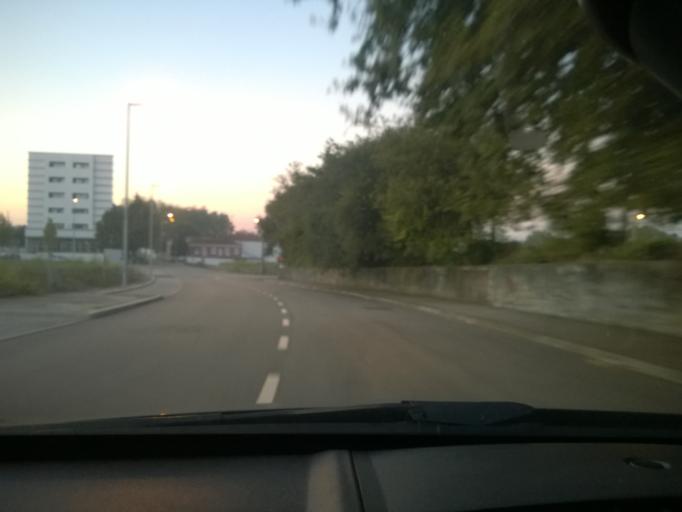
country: PT
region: Porto
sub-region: Maia
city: Anta
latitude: 41.2625
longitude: -8.6119
